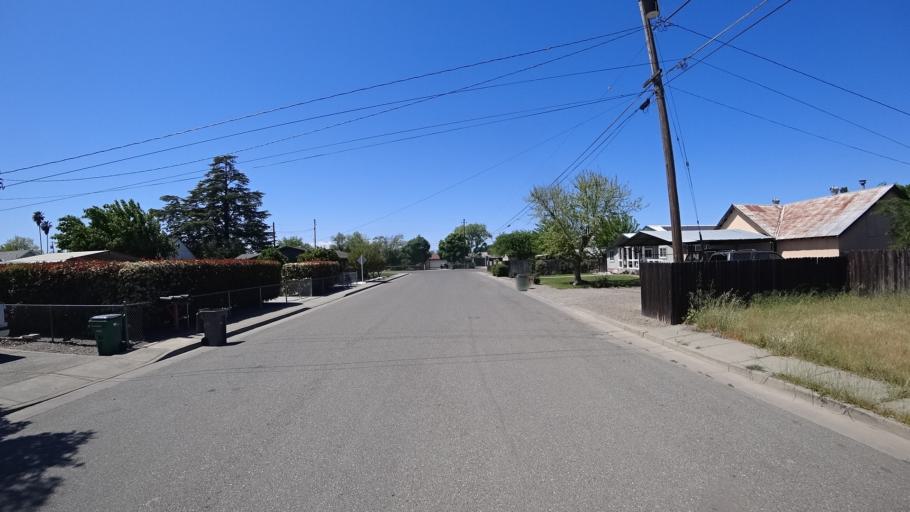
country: US
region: California
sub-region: Glenn County
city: Orland
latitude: 39.7455
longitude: -122.1813
